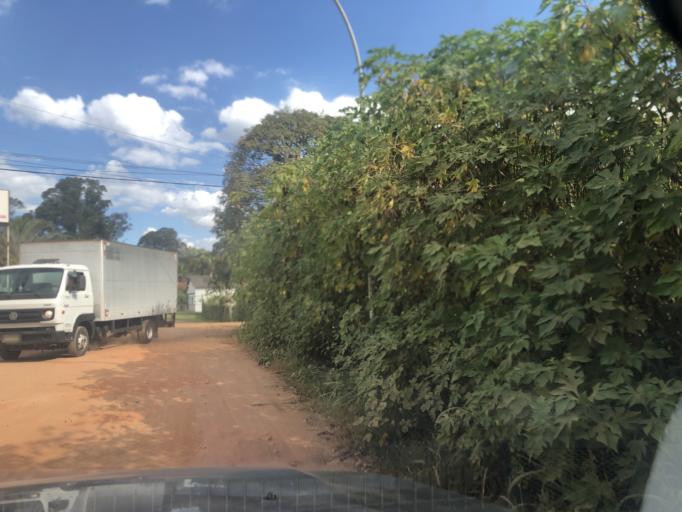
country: BR
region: Federal District
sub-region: Brasilia
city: Brasilia
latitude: -15.8755
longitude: -47.9698
